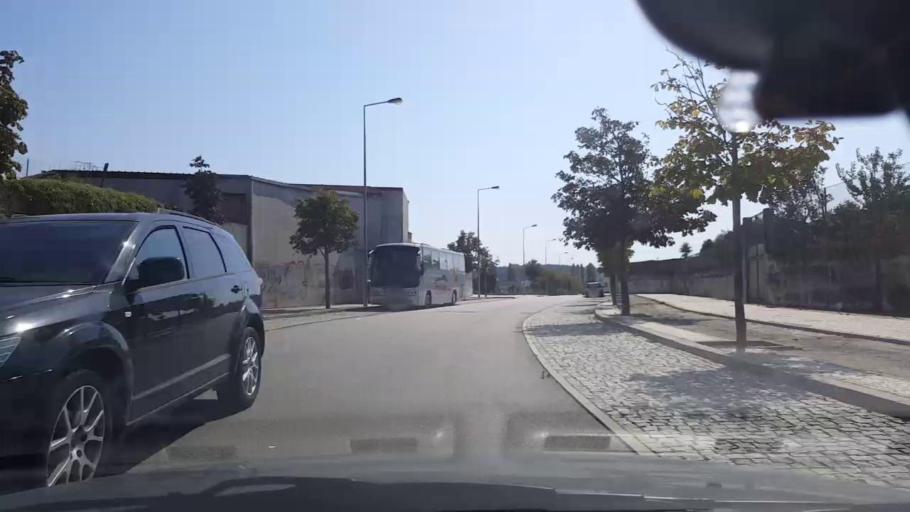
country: PT
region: Porto
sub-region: Vila do Conde
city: Vila do Conde
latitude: 41.3623
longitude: -8.7326
